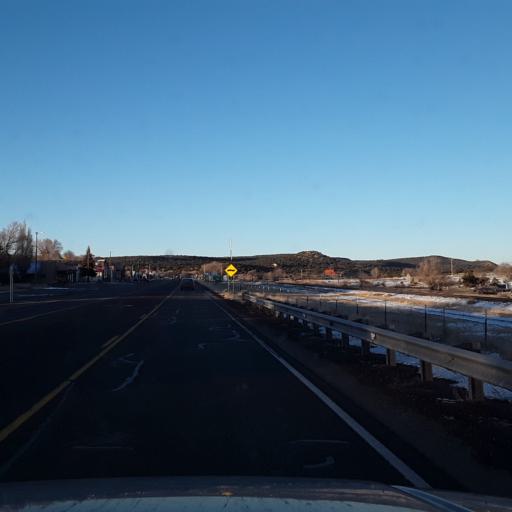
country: US
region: New Mexico
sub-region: Lincoln County
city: Carrizozo
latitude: 34.2465
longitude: -105.5949
